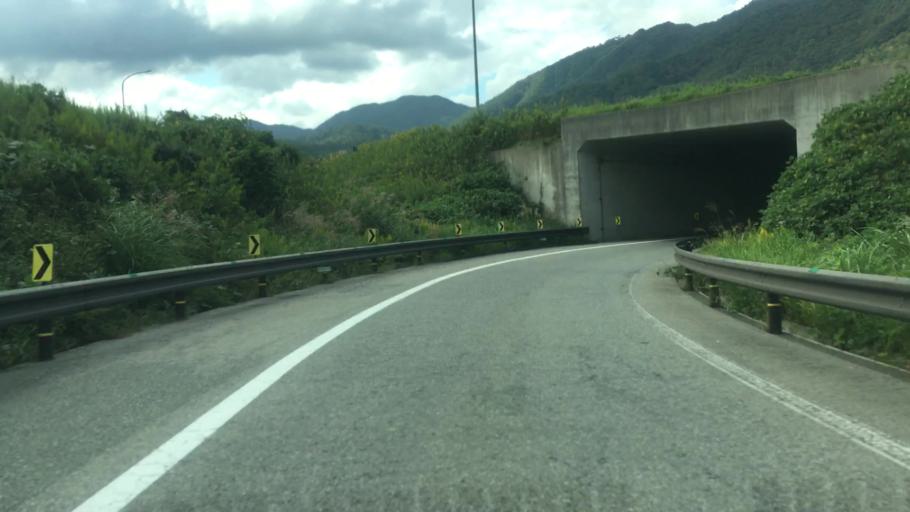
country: JP
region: Hyogo
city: Toyooka
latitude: 35.3121
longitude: 134.8429
